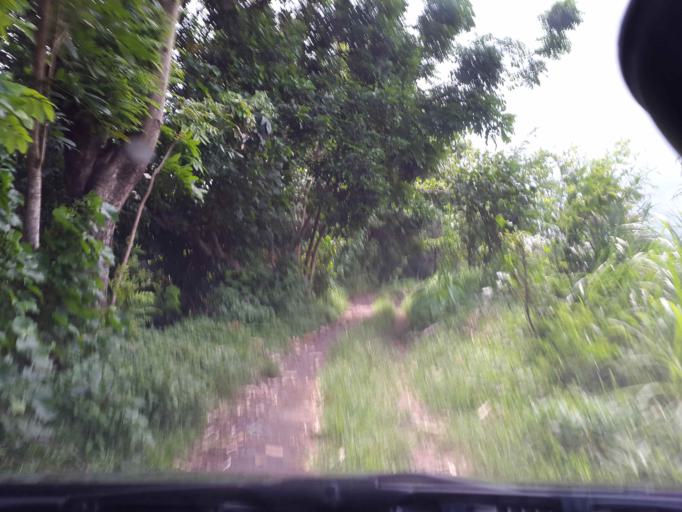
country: ID
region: West Nusa Tenggara
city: Batukuta
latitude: -8.6046
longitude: 116.1891
